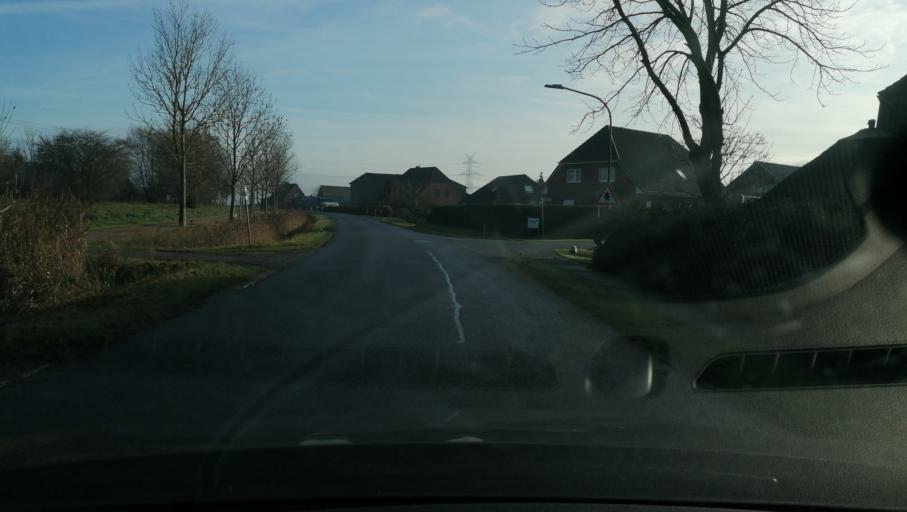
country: DE
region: Schleswig-Holstein
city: Epenwohrden
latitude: 54.1063
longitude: 9.0352
